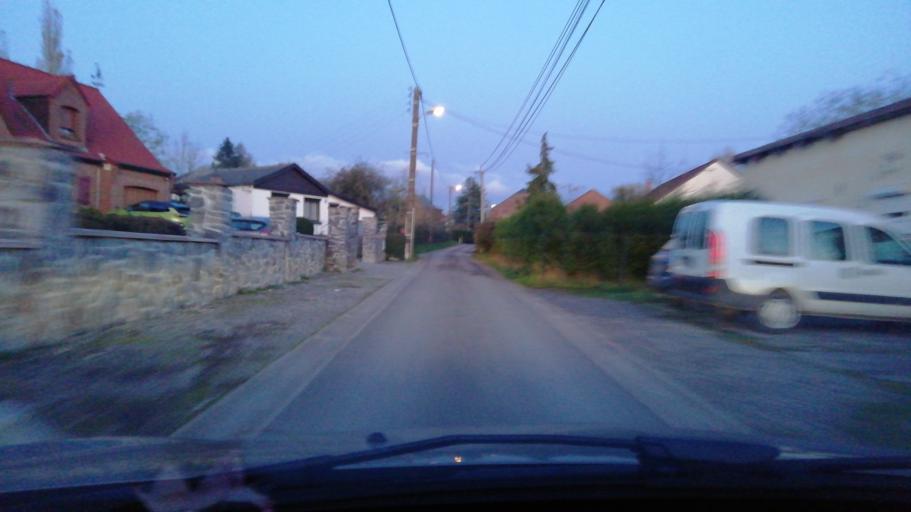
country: FR
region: Nord-Pas-de-Calais
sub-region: Departement du Nord
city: Marpent
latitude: 50.2574
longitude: 4.0843
